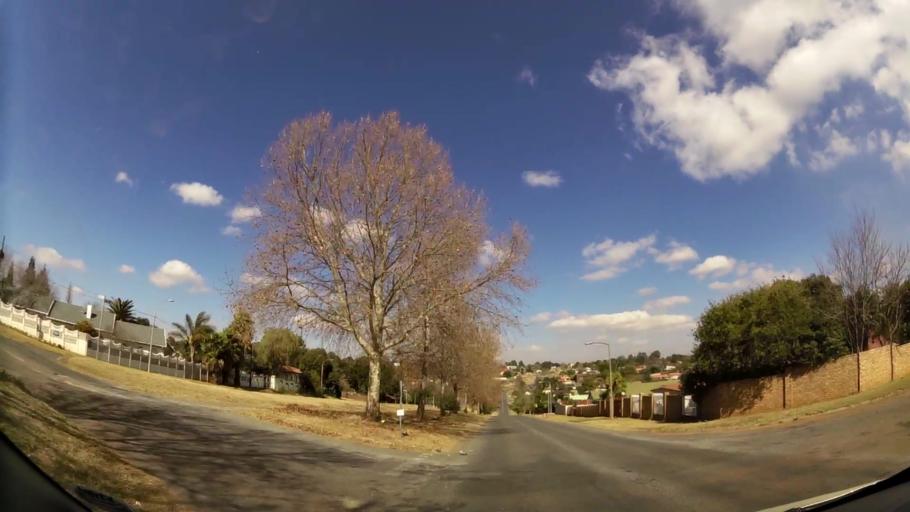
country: ZA
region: Gauteng
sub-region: City of Johannesburg Metropolitan Municipality
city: Roodepoort
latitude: -26.1210
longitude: 27.8384
